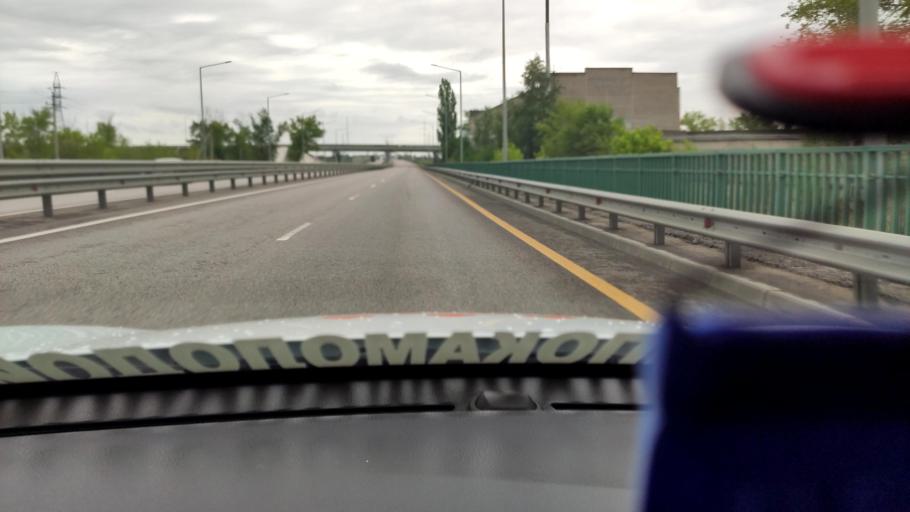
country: RU
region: Voronezj
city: Novaya Usman'
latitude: 51.6304
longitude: 39.3183
